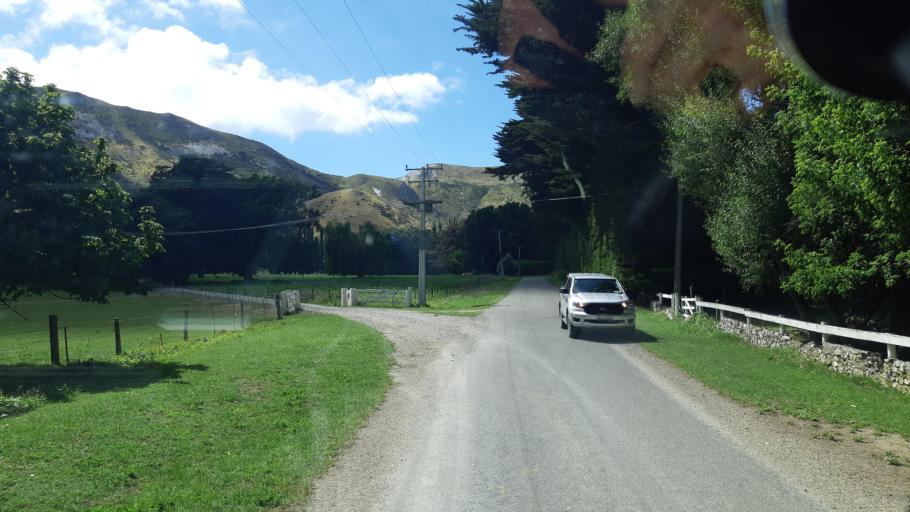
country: NZ
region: Marlborough
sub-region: Marlborough District
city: Blenheim
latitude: -41.8238
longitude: 174.1675
